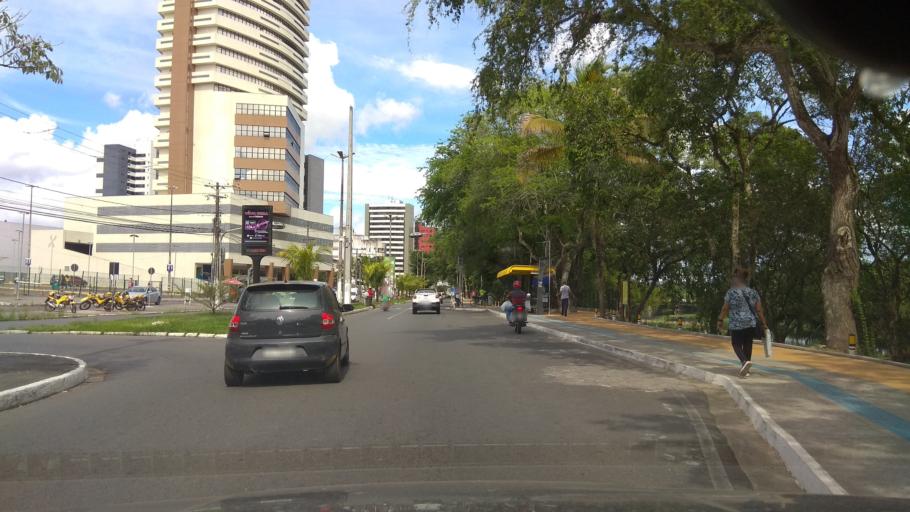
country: BR
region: Bahia
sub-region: Itabuna
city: Itabuna
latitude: -14.7961
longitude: -39.2748
